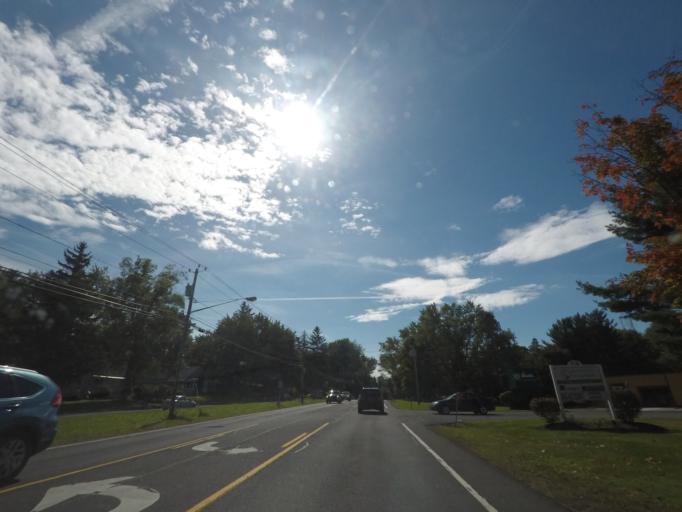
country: US
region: New York
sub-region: Rensselaer County
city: East Greenbush
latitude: 42.6147
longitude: -73.7028
